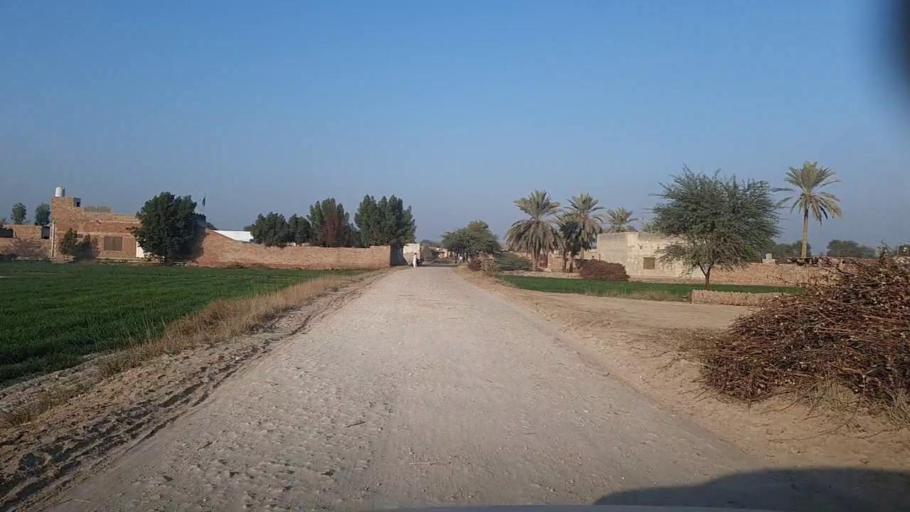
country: PK
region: Sindh
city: Khairpur
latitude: 28.0747
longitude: 69.7451
